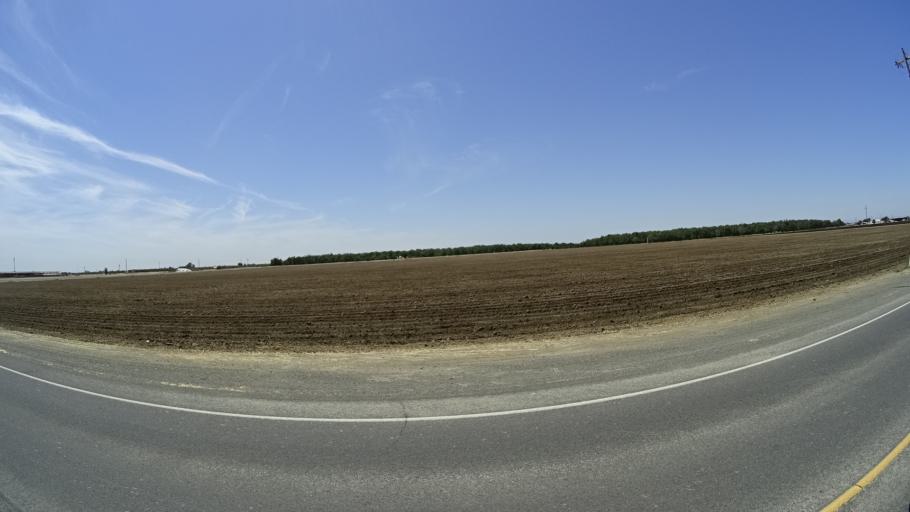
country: US
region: California
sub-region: Kings County
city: Armona
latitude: 36.3426
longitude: -119.7292
